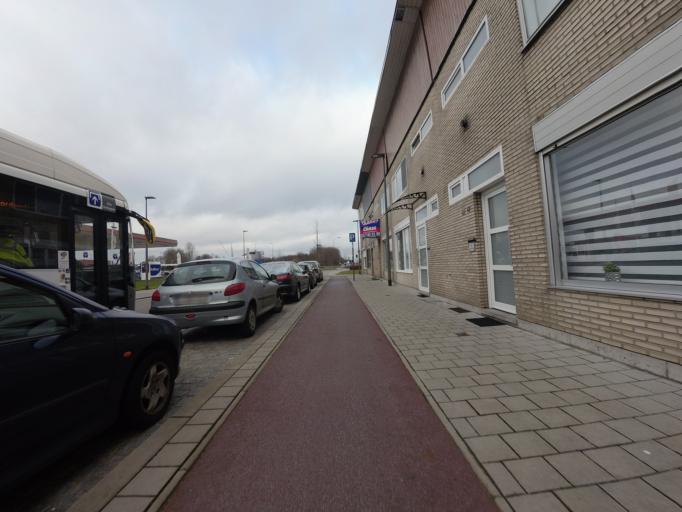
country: BE
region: Flanders
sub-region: Provincie Antwerpen
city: Hoboken
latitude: 51.1910
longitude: 4.3694
